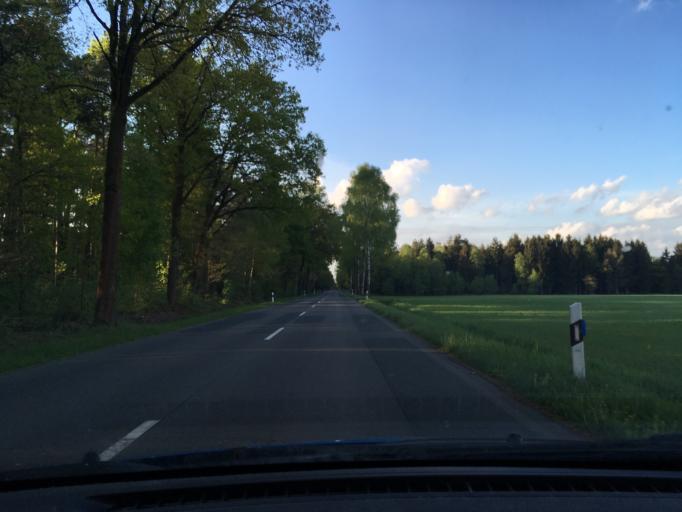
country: DE
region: Lower Saxony
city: Wietzendorf
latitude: 52.8622
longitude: 9.9803
